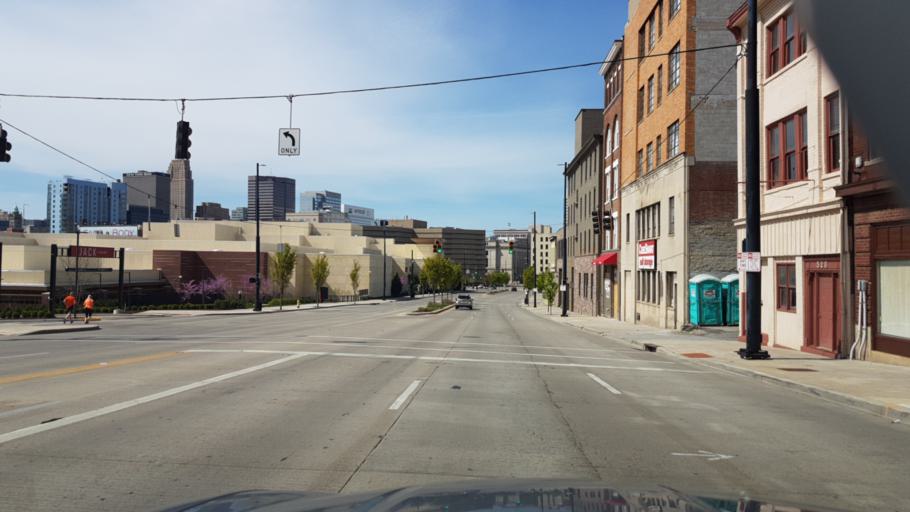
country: US
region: Kentucky
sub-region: Campbell County
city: Newport
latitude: 39.1098
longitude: -84.5046
